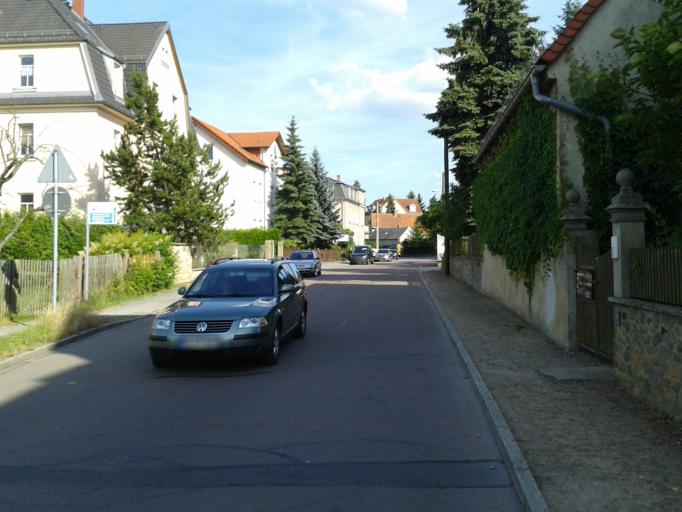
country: DE
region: Saxony
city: Albertstadt
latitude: 51.1114
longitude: 13.7684
